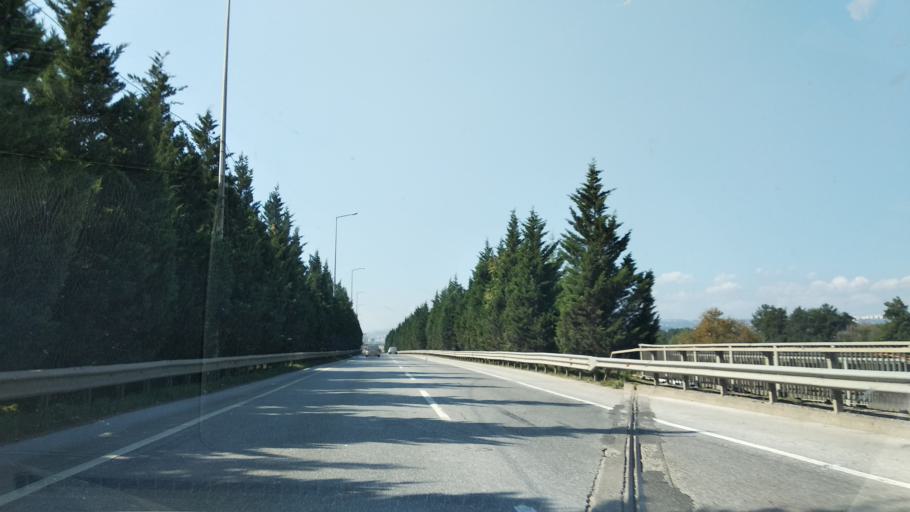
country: TR
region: Kocaeli
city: Kosekoy
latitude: 40.7557
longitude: 30.0087
